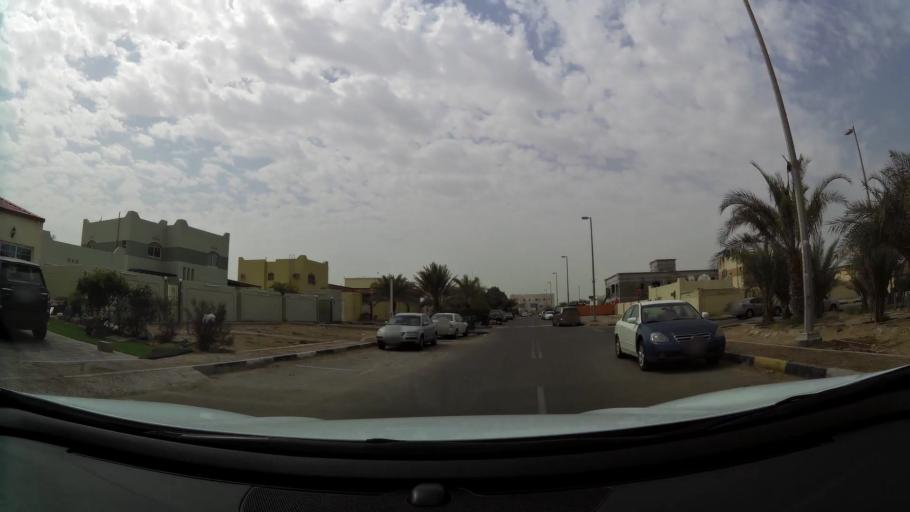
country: AE
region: Abu Dhabi
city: Abu Dhabi
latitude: 24.3102
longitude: 54.6402
